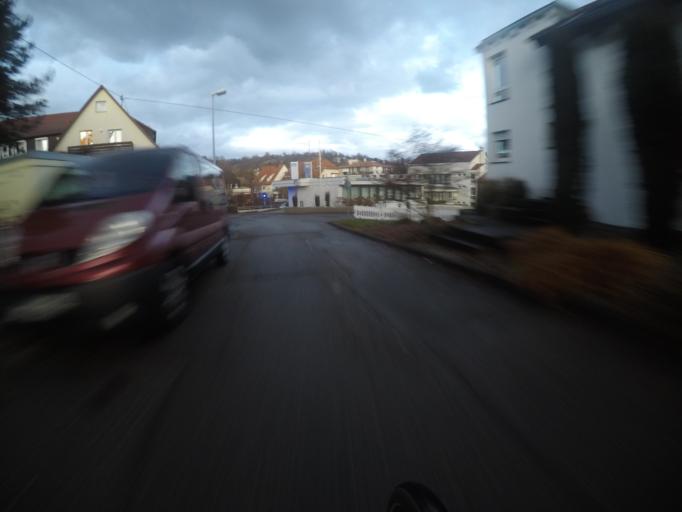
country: DE
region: Baden-Wuerttemberg
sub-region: Tuebingen Region
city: Dettenhausen
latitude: 48.6078
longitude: 9.0989
